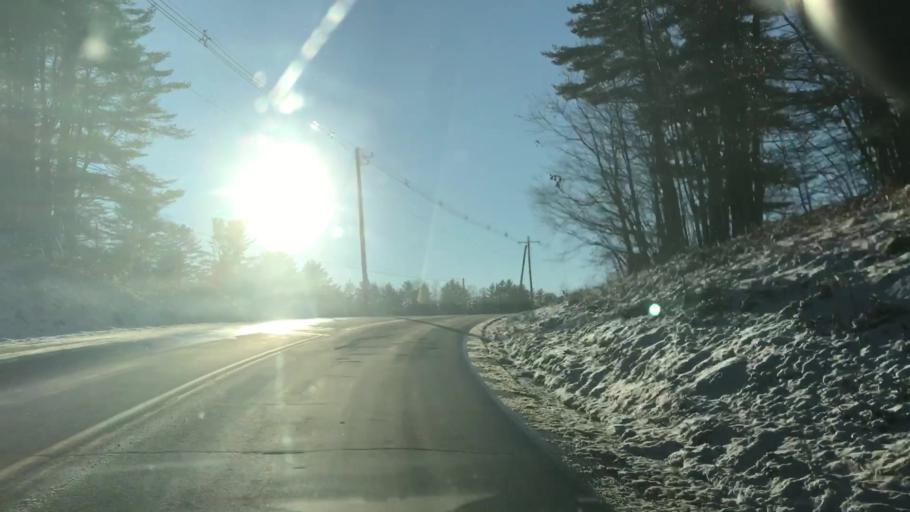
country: US
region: New Hampshire
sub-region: Grafton County
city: North Haverhill
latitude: 44.0722
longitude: -72.0325
